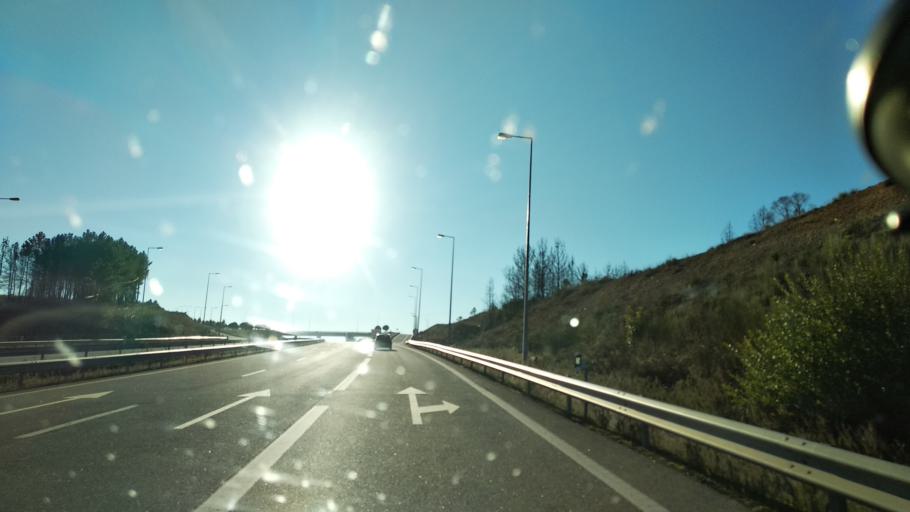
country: PT
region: Santarem
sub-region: Macao
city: Macao
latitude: 39.5169
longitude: -8.0086
